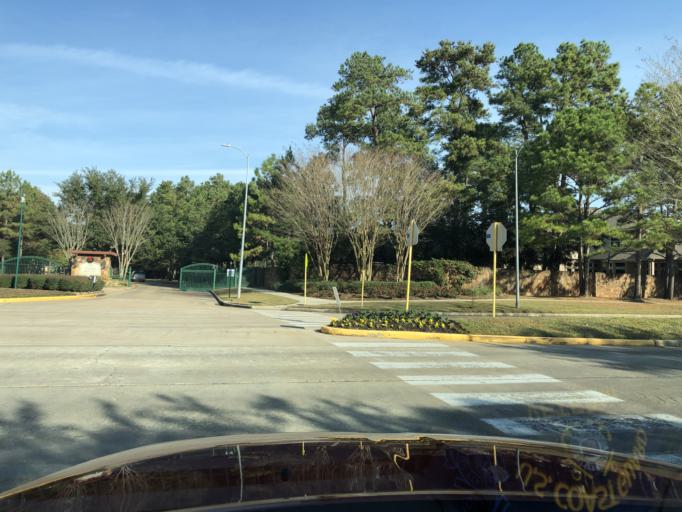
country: US
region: Texas
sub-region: Harris County
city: Tomball
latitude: 30.0331
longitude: -95.5672
